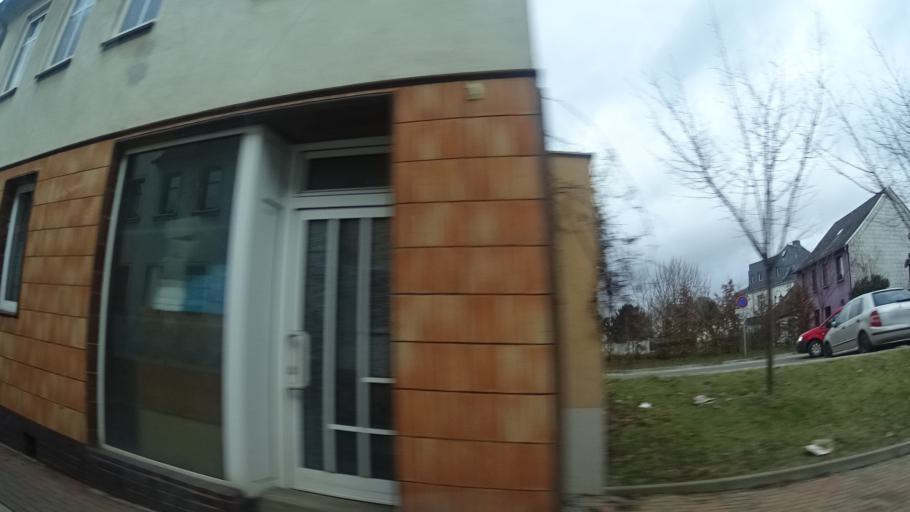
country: DE
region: Thuringia
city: Zeulenroda
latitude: 50.6461
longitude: 11.9815
